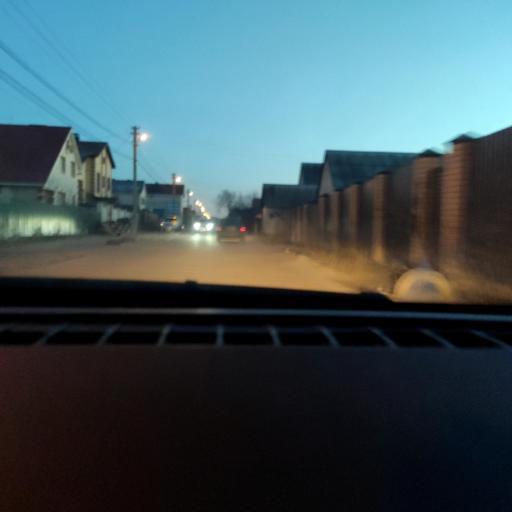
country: RU
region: Voronezj
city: Podgornoye
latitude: 51.7435
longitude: 39.1622
